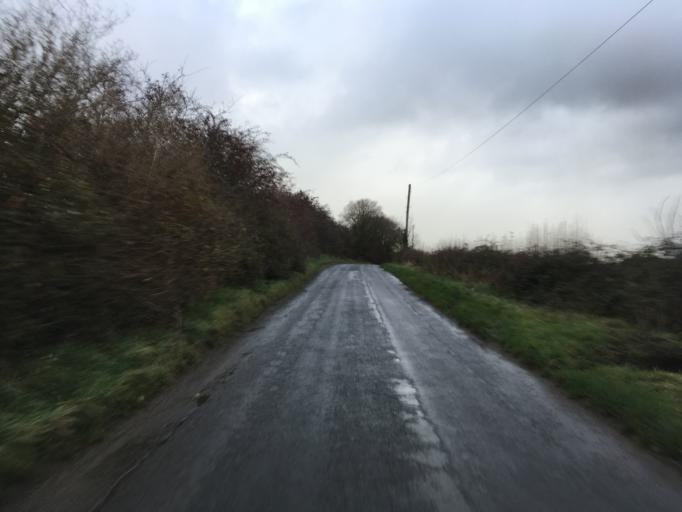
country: GB
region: England
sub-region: Wiltshire
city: Nettleton
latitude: 51.5096
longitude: -2.2903
